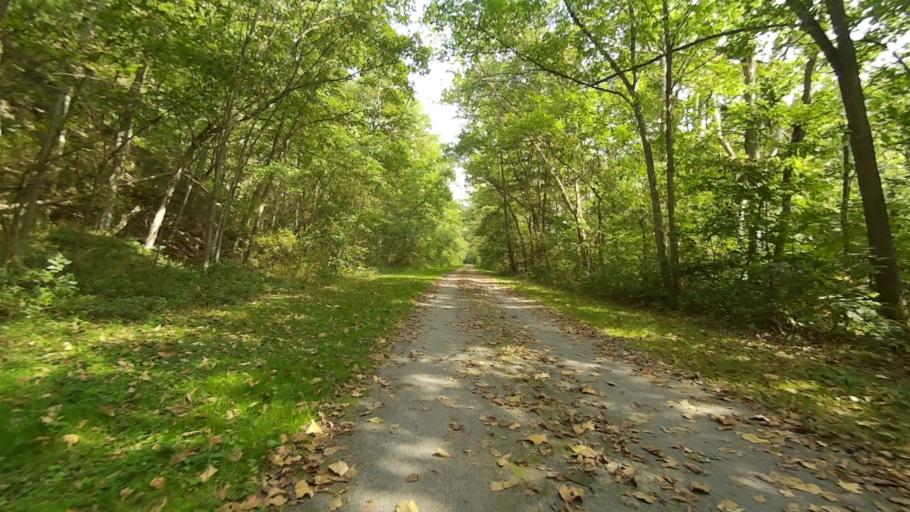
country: US
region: Pennsylvania
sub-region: Blair County
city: Williamsburg
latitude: 40.5014
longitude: -78.1663
